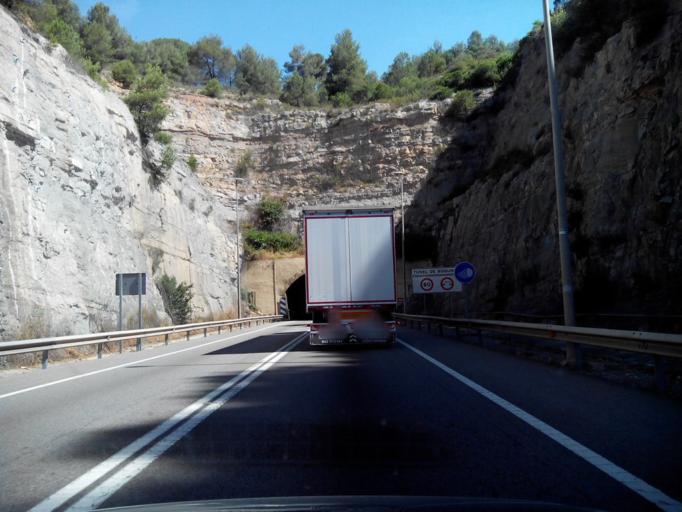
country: ES
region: Catalonia
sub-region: Provincia de Barcelona
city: Monistrol de Montserrat
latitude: 41.6268
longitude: 1.8479
